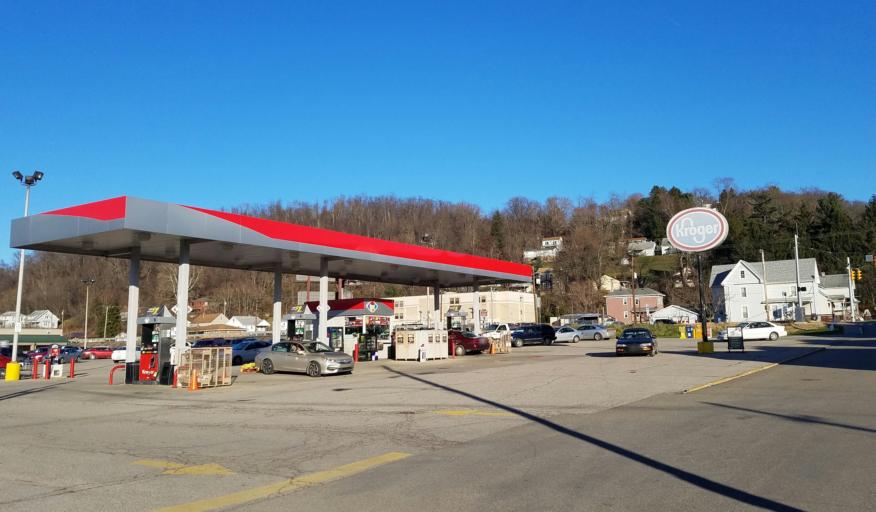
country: US
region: West Virginia
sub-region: Brooke County
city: Wellsburg
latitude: 40.2893
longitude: -80.6093
